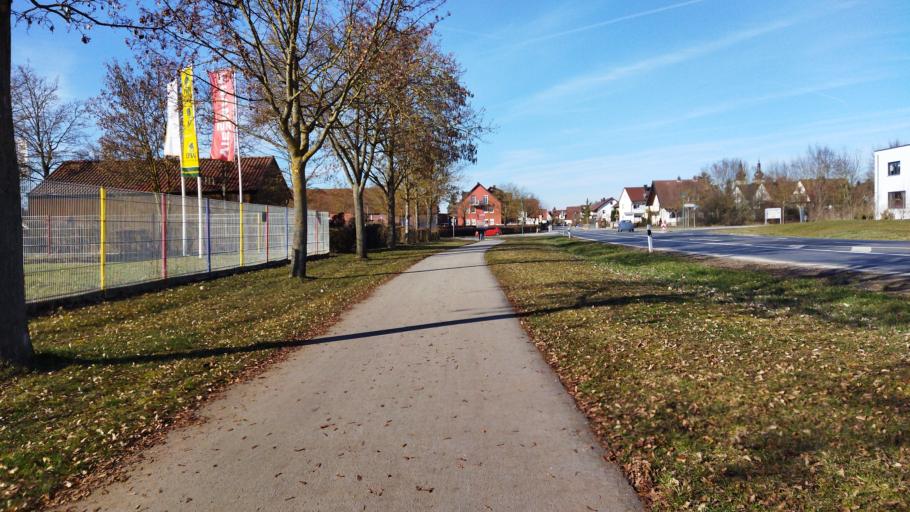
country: DE
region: Bavaria
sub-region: Regierungsbezirk Unterfranken
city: Grafenrheinfeld
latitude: 49.9953
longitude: 10.1986
